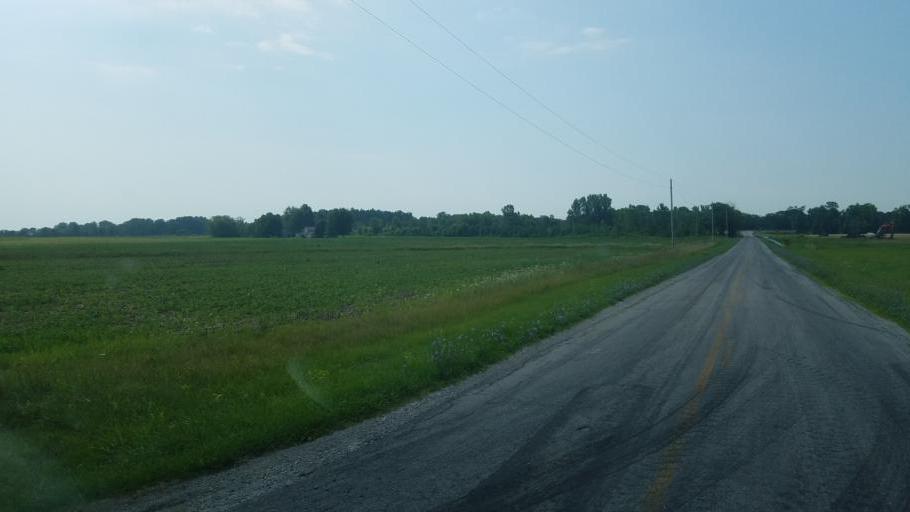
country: US
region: Ohio
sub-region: Hardin County
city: Kenton
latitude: 40.5999
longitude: -83.4095
